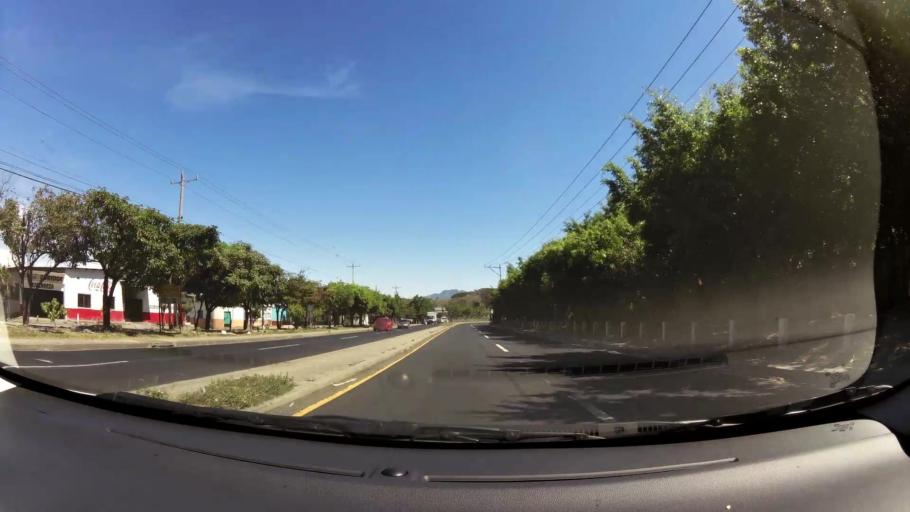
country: SV
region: La Libertad
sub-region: Distrito de Quezaltepeque
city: Quezaltepeque
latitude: 13.8265
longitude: -89.2671
